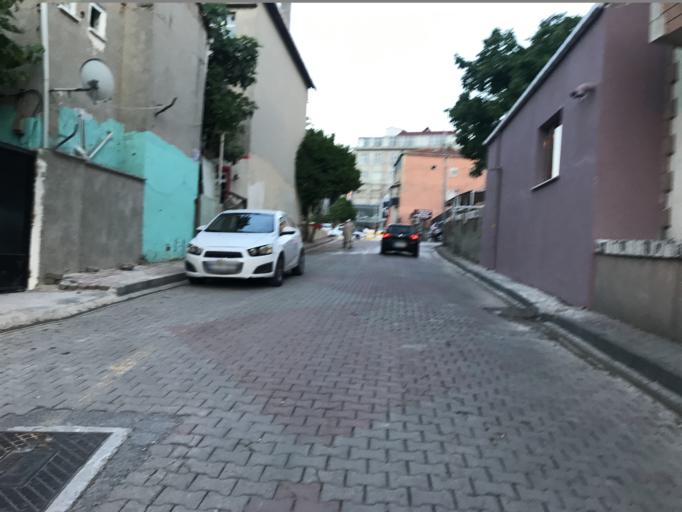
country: TR
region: Istanbul
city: Istanbul
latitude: 41.0392
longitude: 28.9288
